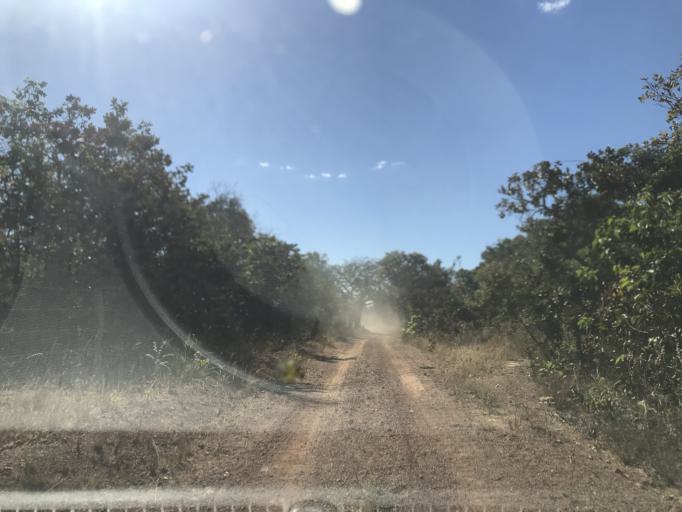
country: BR
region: Goias
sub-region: Padre Bernardo
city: Padre Bernardo
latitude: -15.4080
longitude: -48.2286
